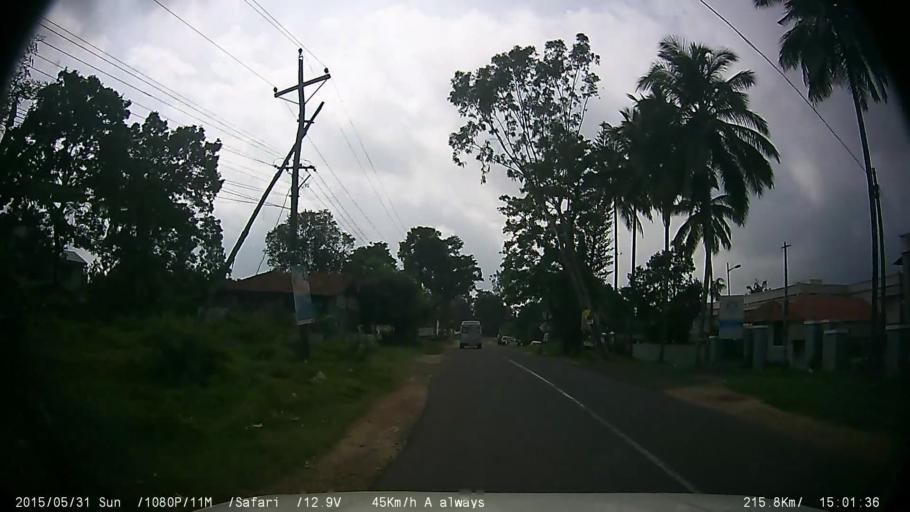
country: IN
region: Kerala
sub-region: Wayanad
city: Kalpetta
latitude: 11.6237
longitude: 76.2109
